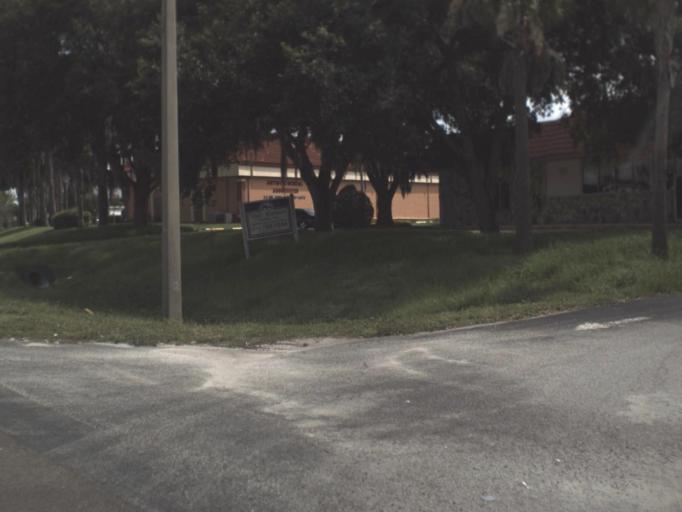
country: US
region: Florida
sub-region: Pasco County
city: Zephyrhills
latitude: 28.2464
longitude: -82.1898
